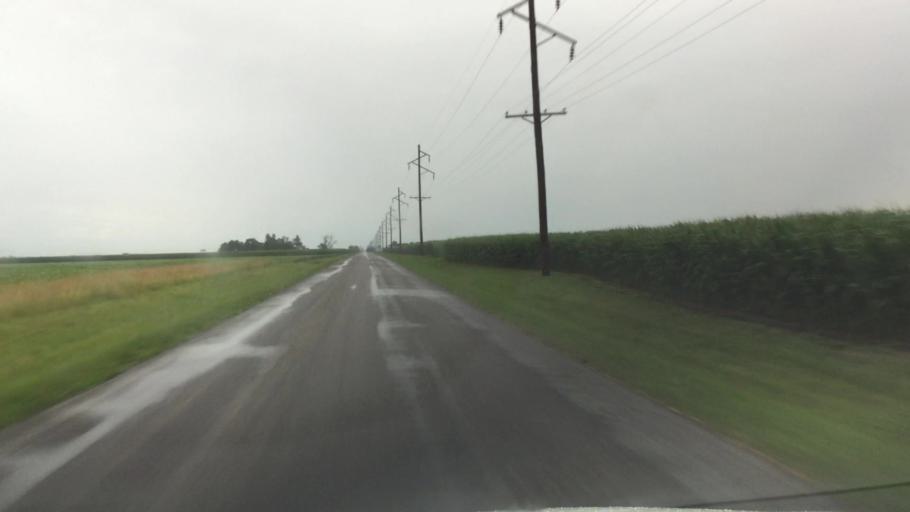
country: US
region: Illinois
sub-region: Hancock County
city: Nauvoo
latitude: 40.5147
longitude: -91.2694
